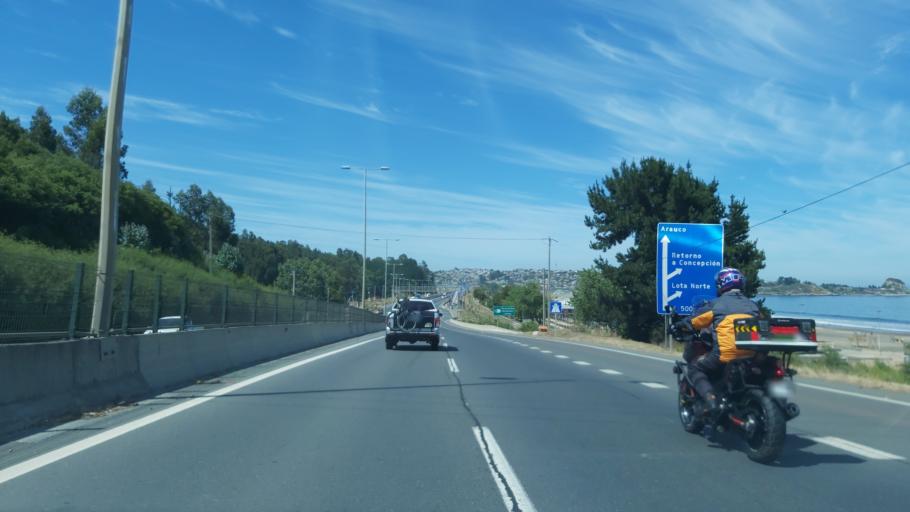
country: CL
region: Biobio
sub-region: Provincia de Concepcion
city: Coronel
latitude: -37.0598
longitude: -73.1402
